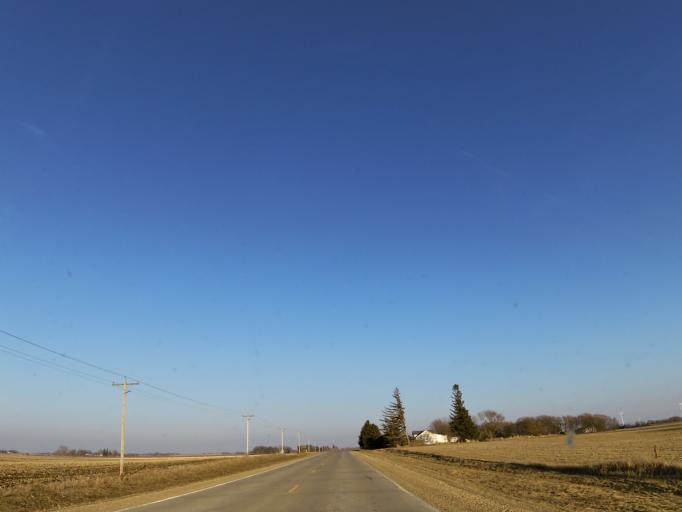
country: US
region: Iowa
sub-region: Worth County
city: Northwood
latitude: 43.4378
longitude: -93.1044
